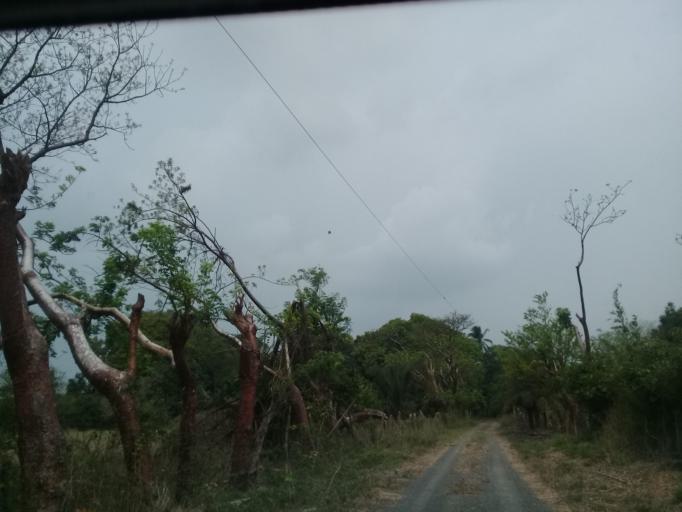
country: MX
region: Veracruz
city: Jamapa
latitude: 19.0500
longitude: -96.2014
